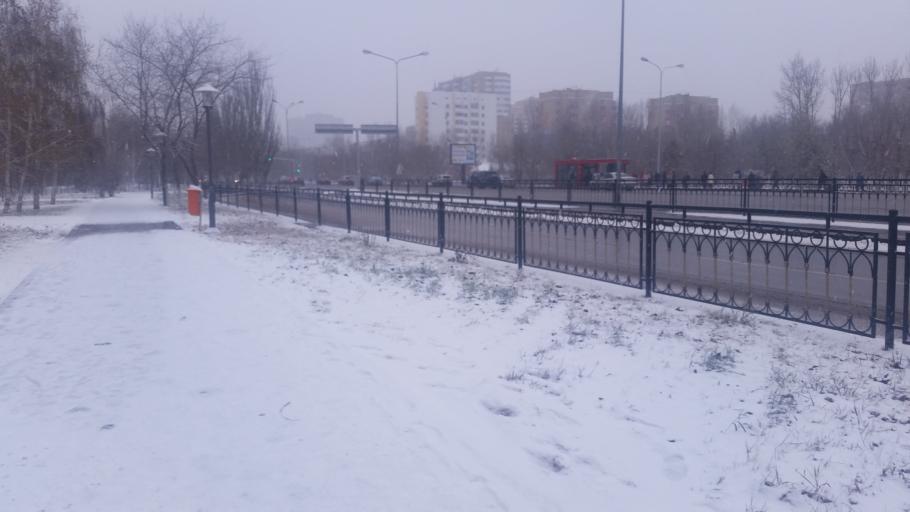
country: KZ
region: Astana Qalasy
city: Astana
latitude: 51.1574
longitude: 71.4776
